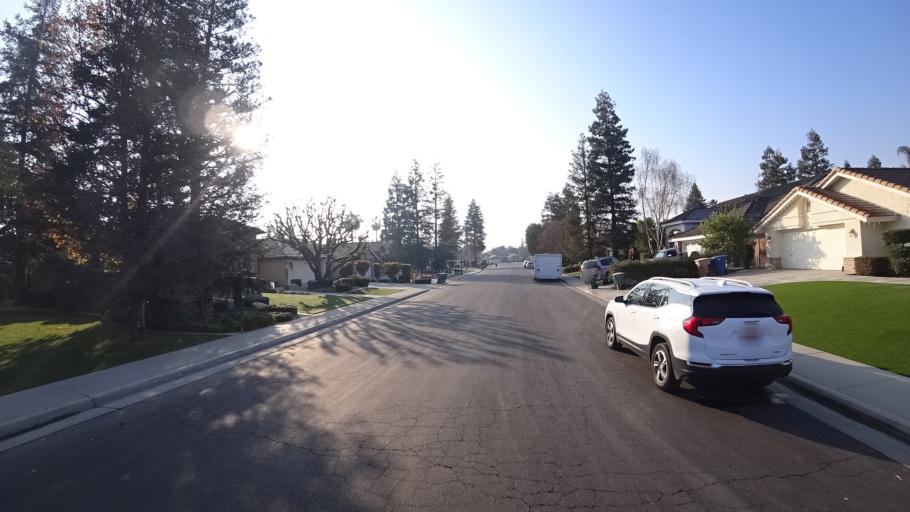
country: US
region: California
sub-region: Kern County
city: Greenacres
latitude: 35.3309
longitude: -119.0977
